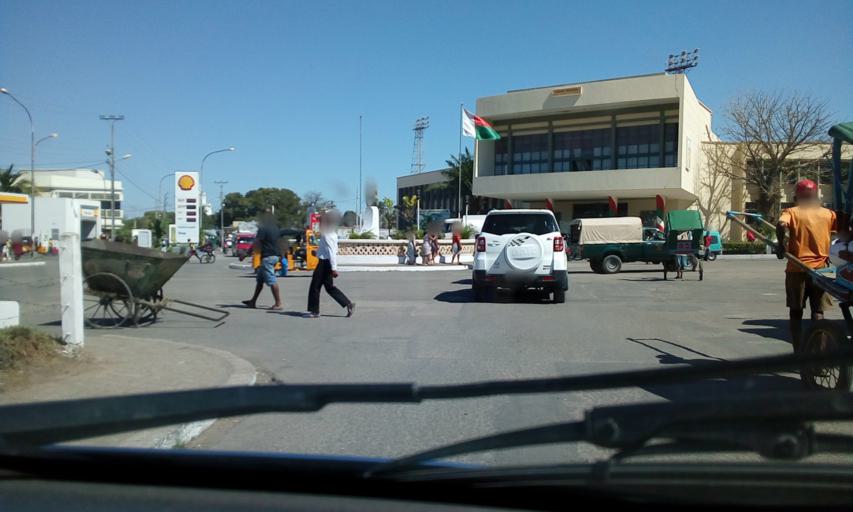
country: MG
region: Boeny
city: Mahajanga
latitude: -15.7180
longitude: 46.3176
